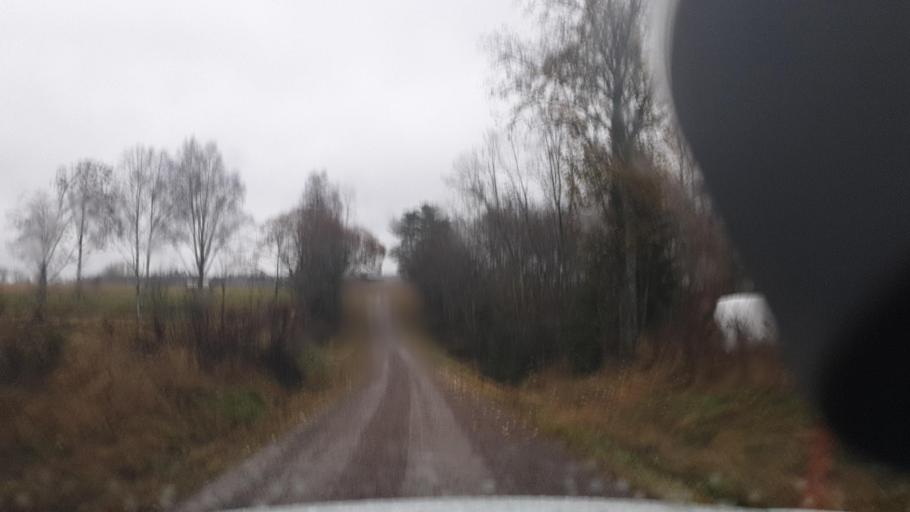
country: SE
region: Vaermland
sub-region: Eda Kommun
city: Charlottenberg
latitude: 59.7411
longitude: 12.1499
